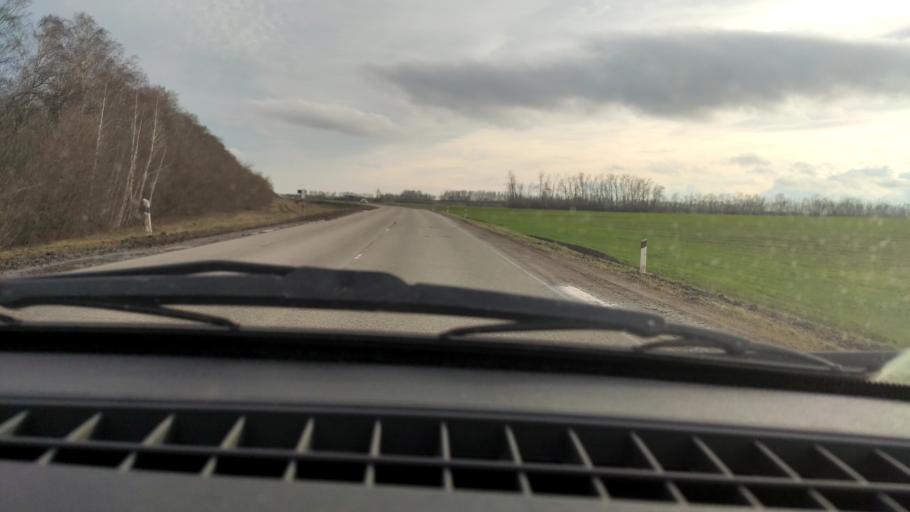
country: RU
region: Bashkortostan
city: Chishmy
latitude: 54.4956
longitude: 55.2787
